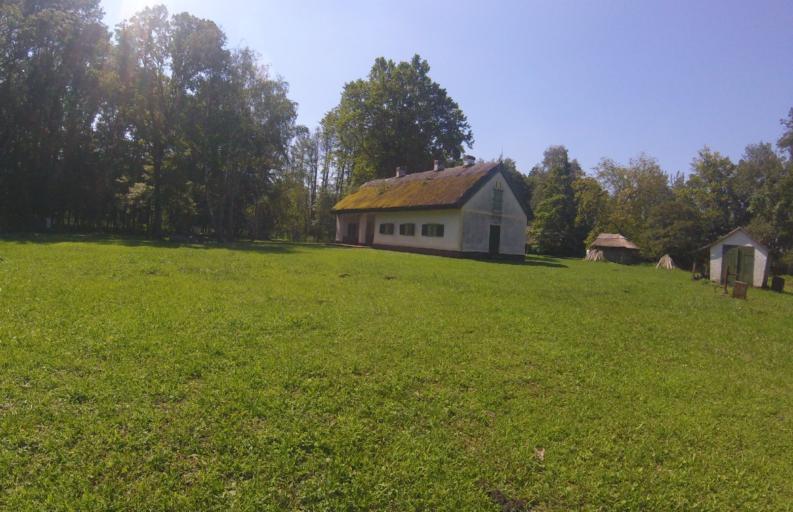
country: HU
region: Zala
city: Sarmellek
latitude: 46.6788
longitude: 17.2301
